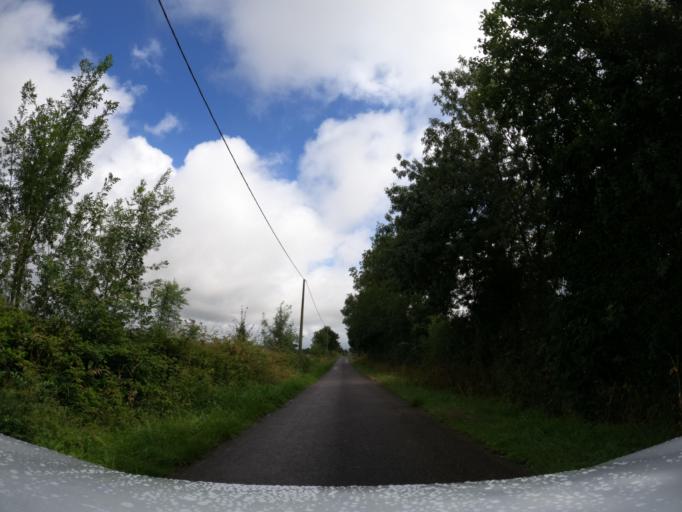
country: FR
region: Pays de la Loire
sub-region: Departement de la Loire-Atlantique
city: Ligne
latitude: 47.4008
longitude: -1.3887
